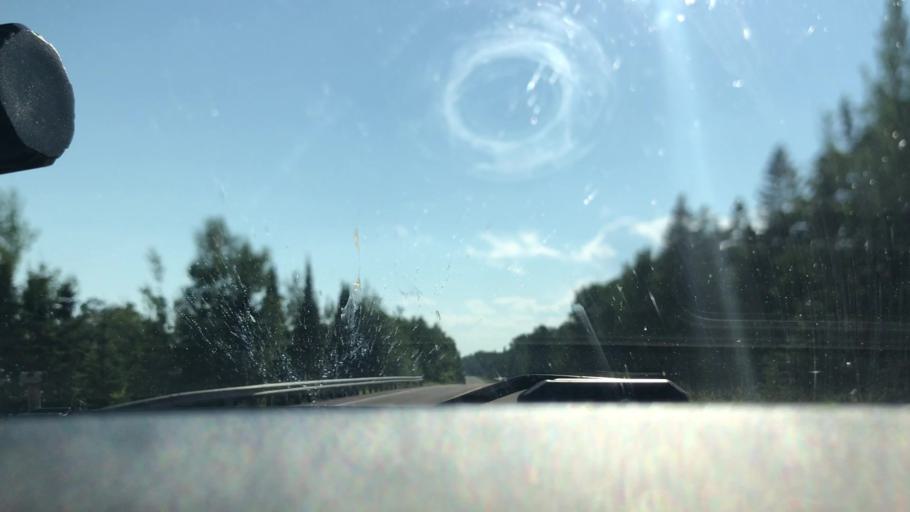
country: US
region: Minnesota
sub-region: Cook County
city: Grand Marais
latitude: 47.8273
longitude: -90.0091
